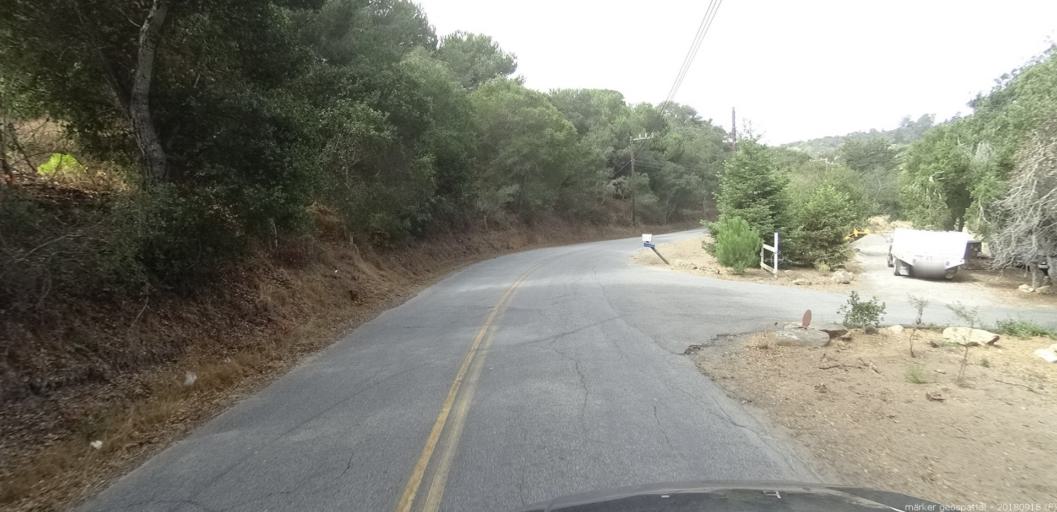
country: US
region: California
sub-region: Monterey County
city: Prunedale
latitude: 36.8019
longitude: -121.6334
